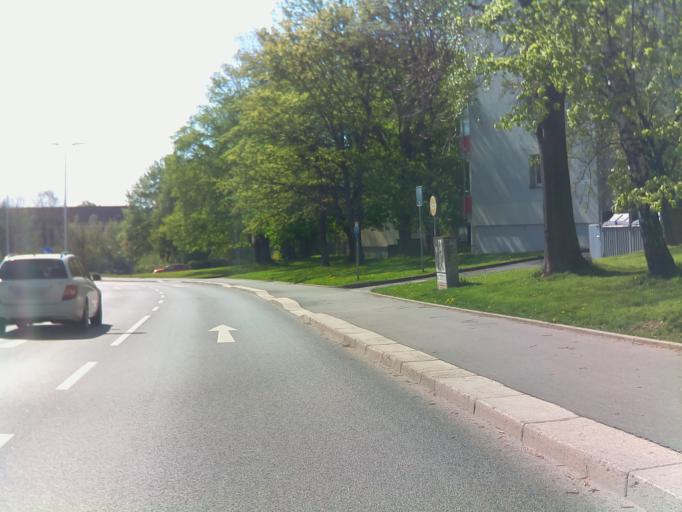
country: DE
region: Saxony
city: Plauen
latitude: 50.5064
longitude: 12.1373
